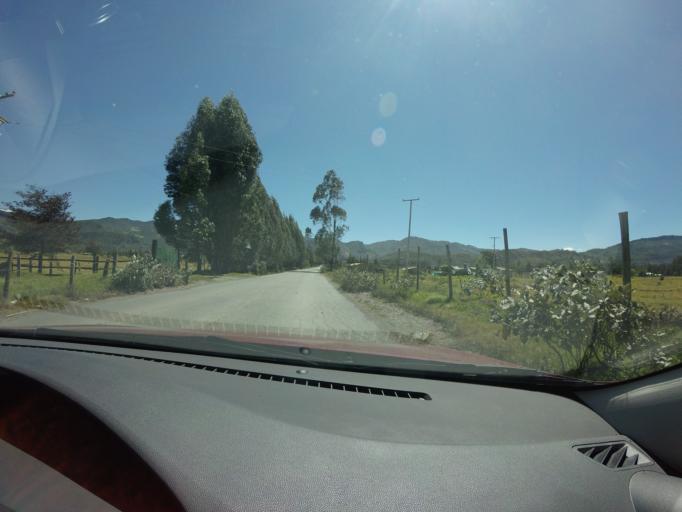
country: CO
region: Cundinamarca
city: Cucunuba
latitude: 5.2605
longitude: -73.7872
